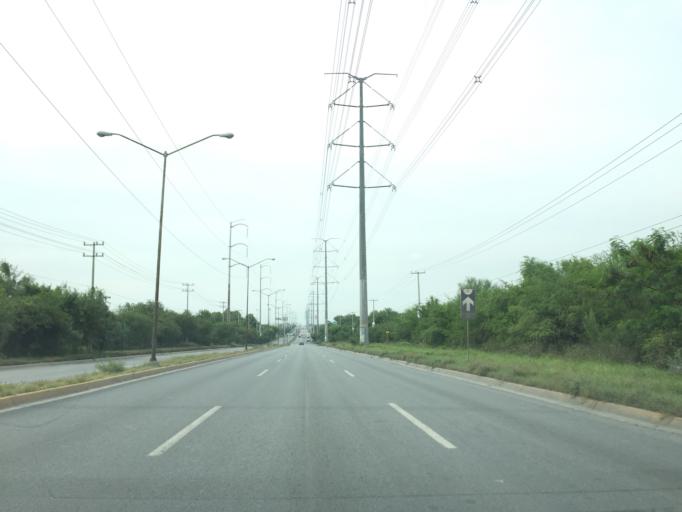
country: MX
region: Nuevo Leon
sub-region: Apodaca
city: Fraccionamiento Cosmopolis Octavo Sector
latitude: 25.7912
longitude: -100.2234
